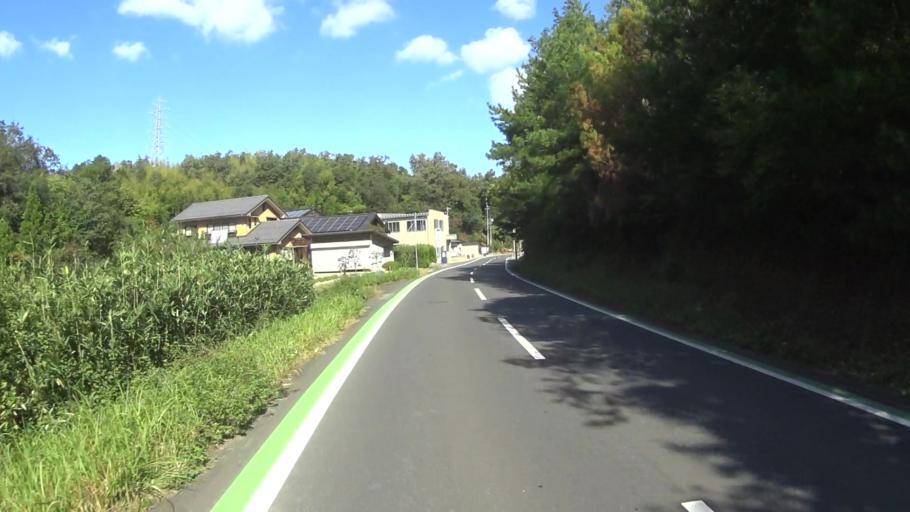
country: JP
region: Kyoto
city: Miyazu
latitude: 35.6381
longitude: 135.0702
